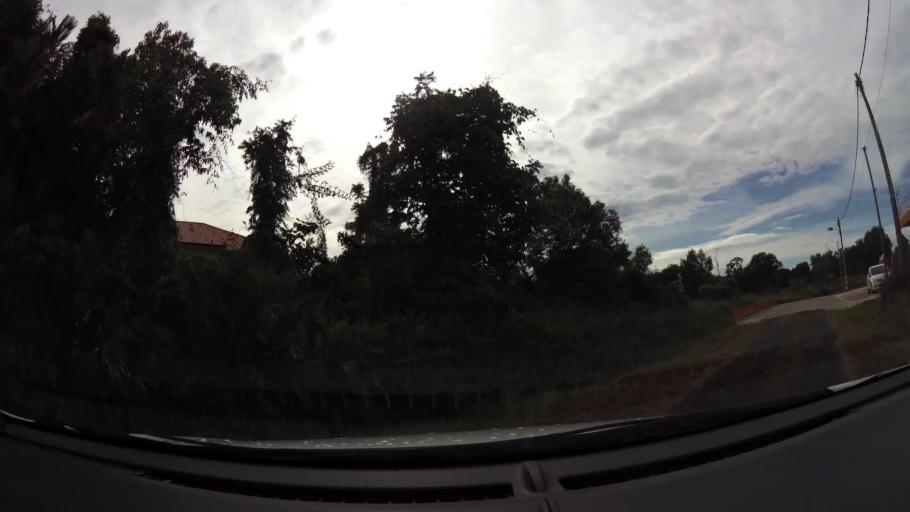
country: BN
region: Belait
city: Seria
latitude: 4.6130
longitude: 114.3625
